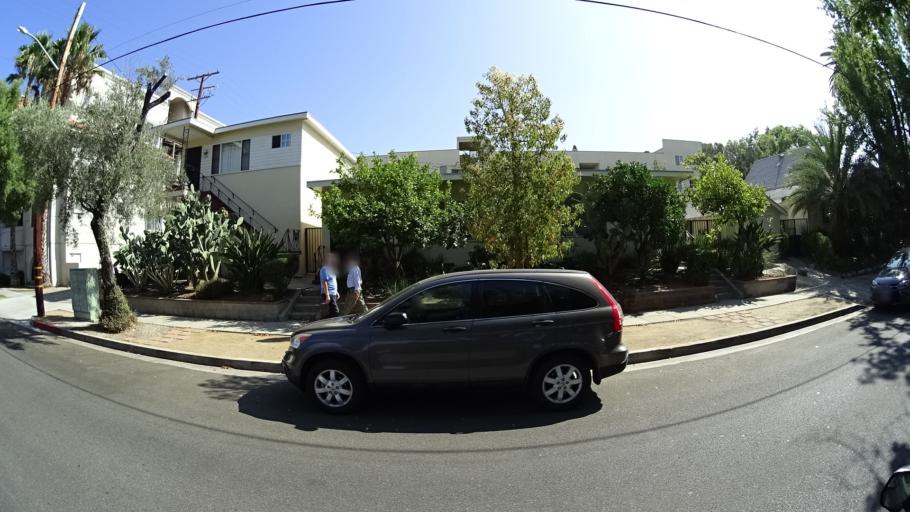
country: US
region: California
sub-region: Los Angeles County
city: Burbank
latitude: 34.1873
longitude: -118.3063
